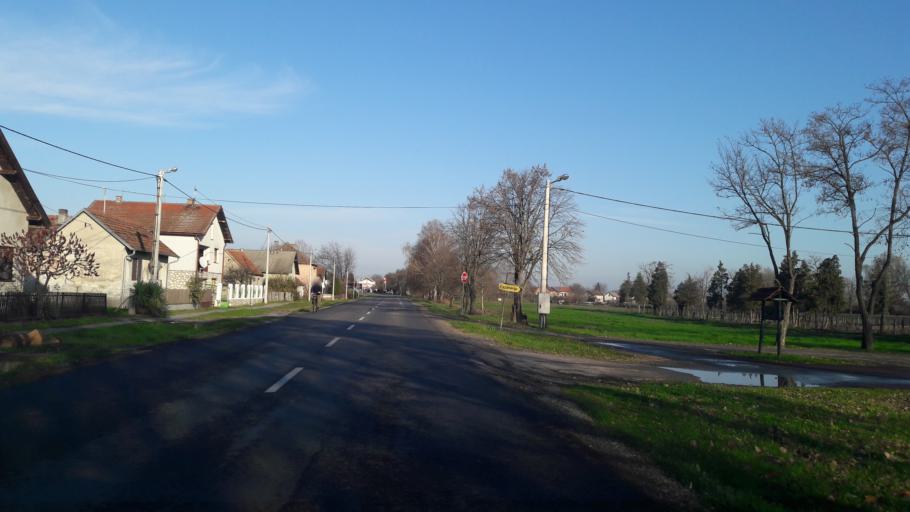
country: HR
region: Osjecko-Baranjska
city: Darda
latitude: 45.6220
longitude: 18.6954
